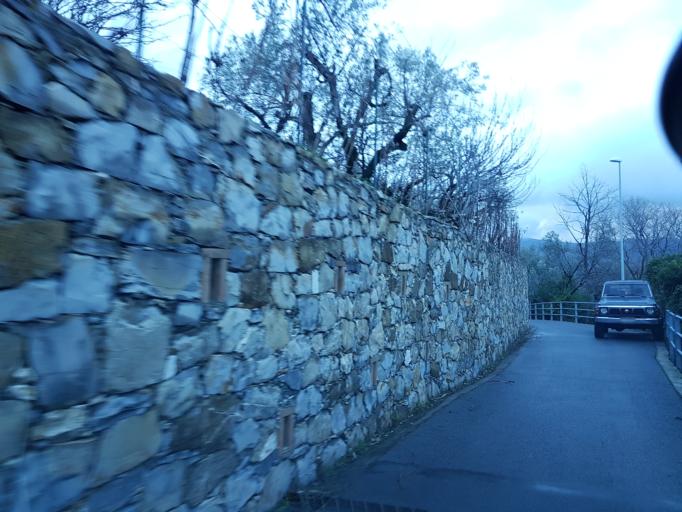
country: IT
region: Liguria
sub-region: Provincia di Genova
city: Genoa
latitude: 44.4334
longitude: 8.9550
